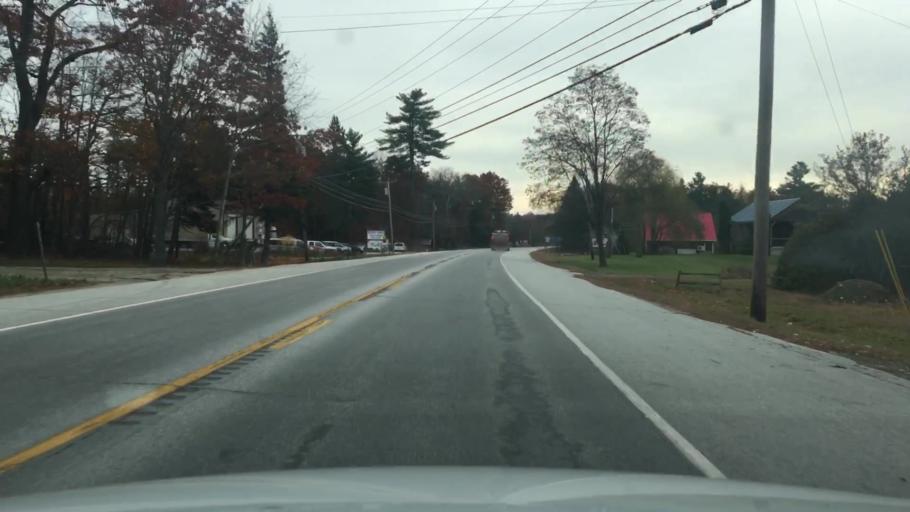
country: US
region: Maine
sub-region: Hancock County
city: Orland
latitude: 44.5667
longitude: -68.7189
